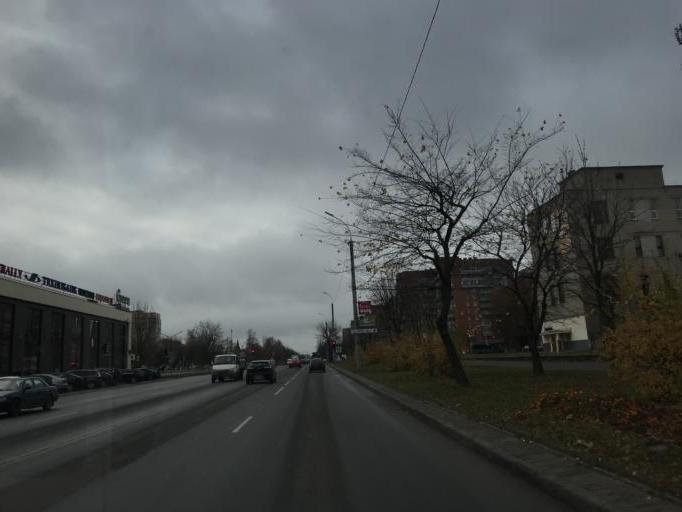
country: BY
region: Mogilev
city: Mahilyow
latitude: 53.8754
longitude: 30.3333
